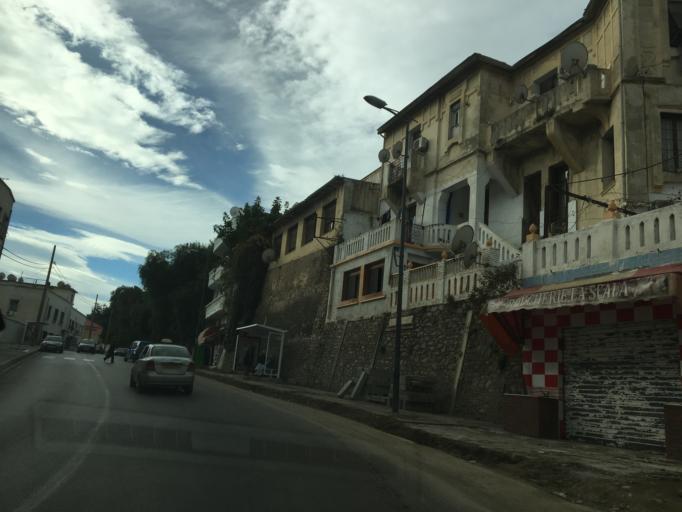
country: DZ
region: Alger
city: Algiers
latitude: 36.7749
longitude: 3.0425
